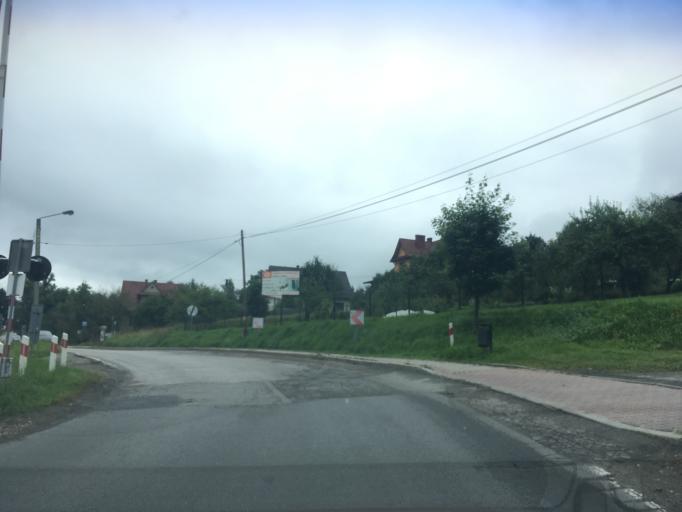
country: PL
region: Lesser Poland Voivodeship
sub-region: Powiat nowotarski
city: Rokiciny
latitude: 49.5885
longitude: 19.9197
